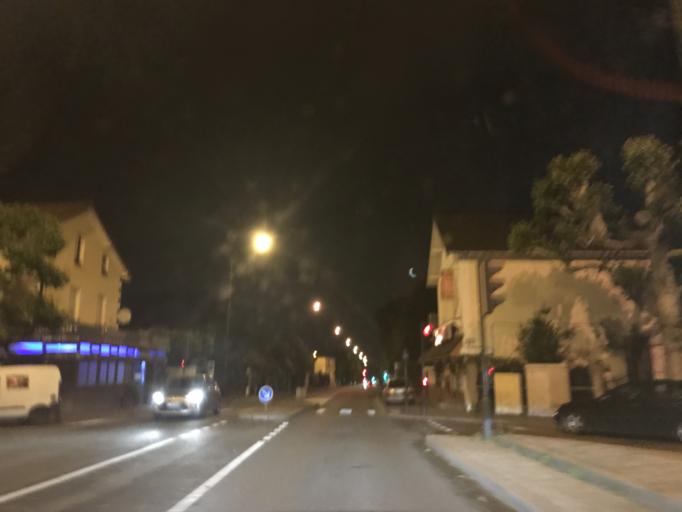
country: FR
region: Ile-de-France
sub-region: Departement des Yvelines
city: Le Mesnil-le-Roi
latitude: 48.9438
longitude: 2.1326
